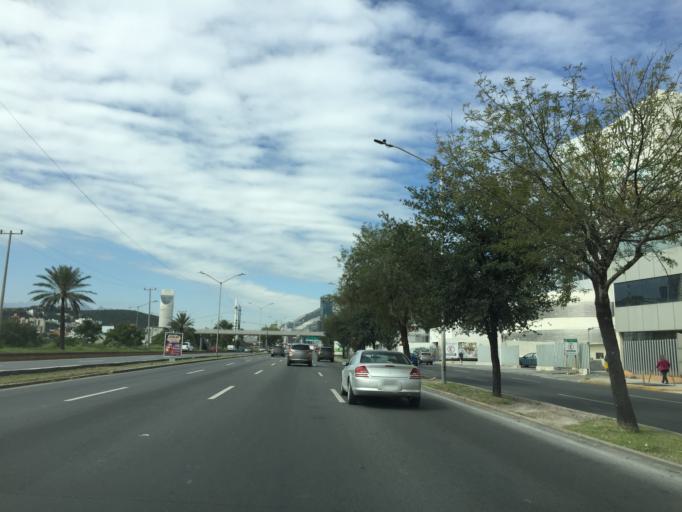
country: MX
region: Nuevo Leon
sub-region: Monterrey
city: Monterrey
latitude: 25.6691
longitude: -100.3404
